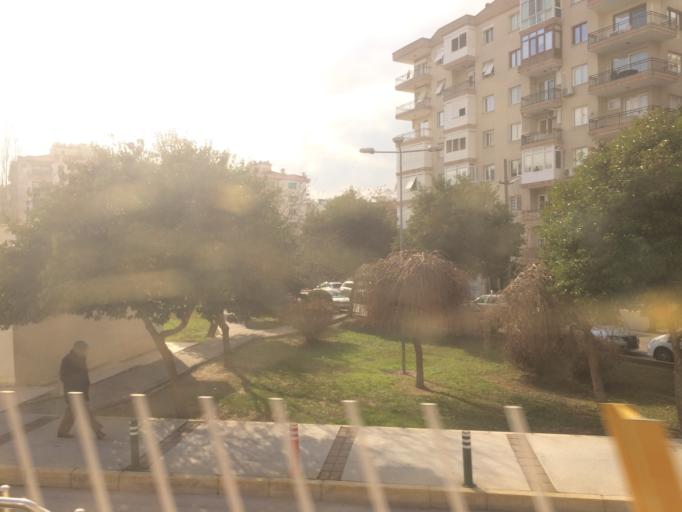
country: TR
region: Izmir
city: Karsiyaka
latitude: 38.4685
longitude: 27.0958
